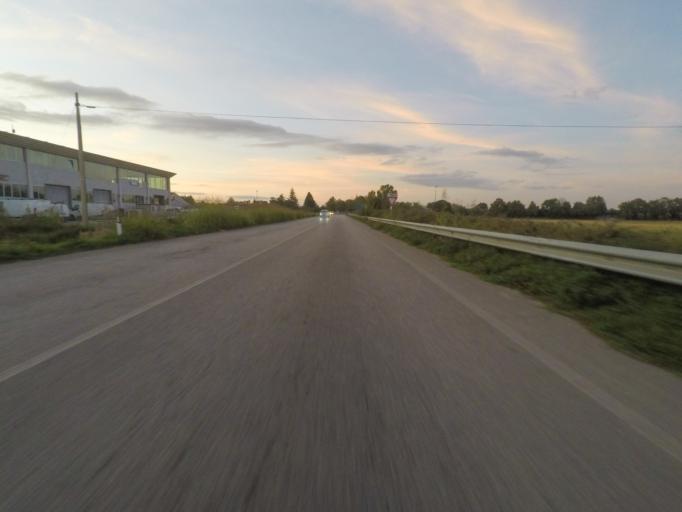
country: IT
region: Tuscany
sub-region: Provincia di Siena
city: Sinalunga
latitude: 43.2196
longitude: 11.7576
